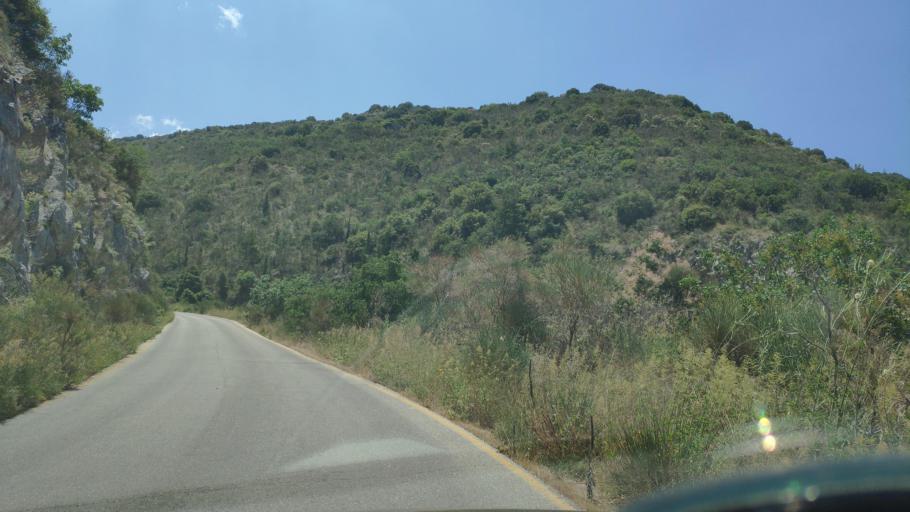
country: GR
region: Ionian Islands
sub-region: Lefkada
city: Nidri
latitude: 38.7451
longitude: 20.6215
